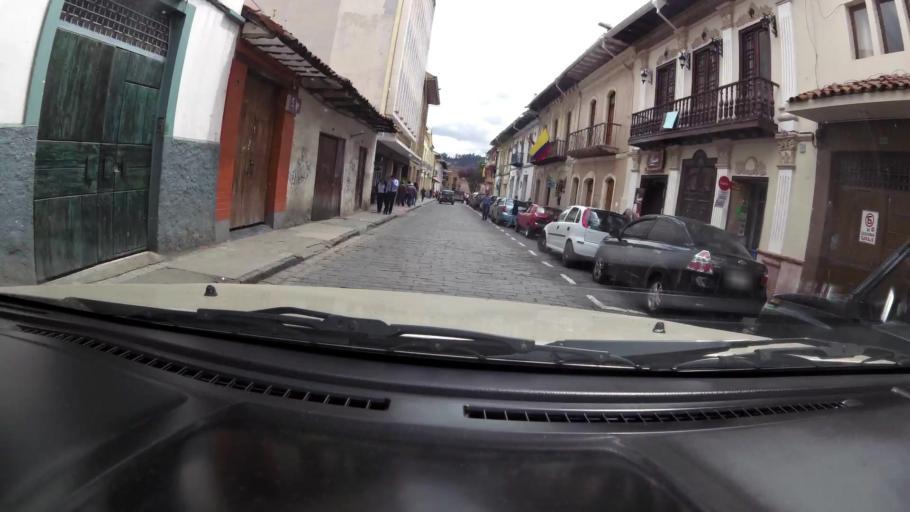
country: EC
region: Azuay
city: Cuenca
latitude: -2.9005
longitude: -79.0036
